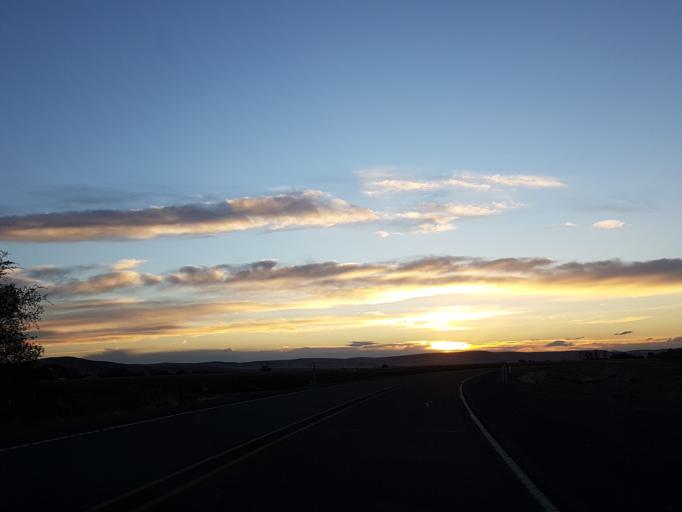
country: US
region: Oregon
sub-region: Malheur County
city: Vale
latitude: 43.9361
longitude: -117.3153
